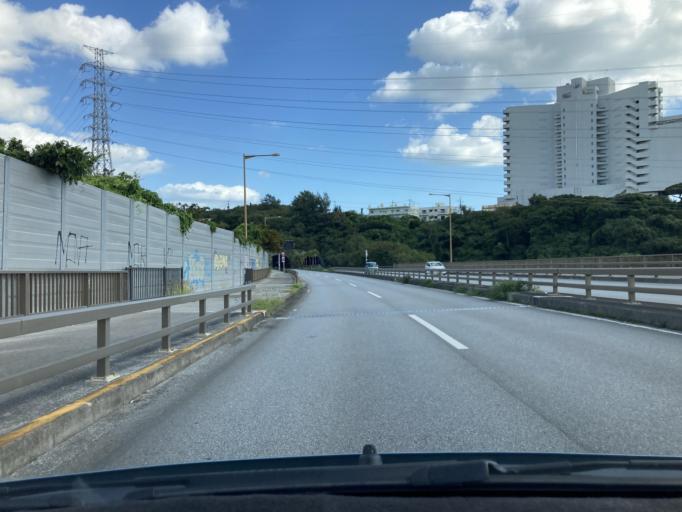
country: JP
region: Okinawa
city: Okinawa
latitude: 26.3150
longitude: 127.8084
